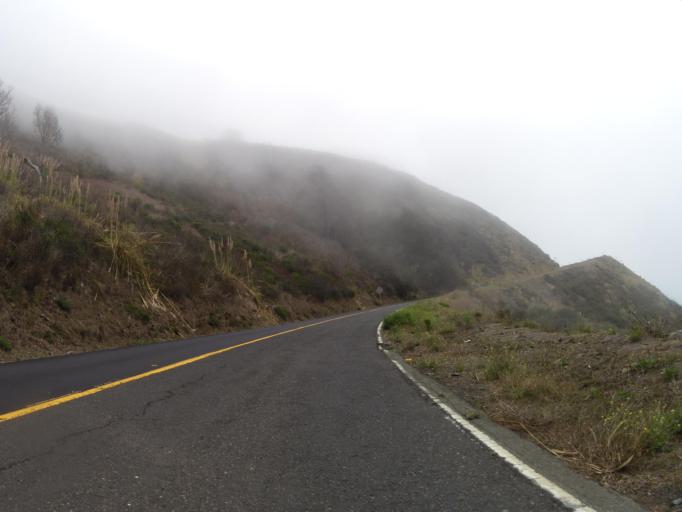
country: US
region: California
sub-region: Sonoma County
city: Monte Rio
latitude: 38.4911
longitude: -123.1915
